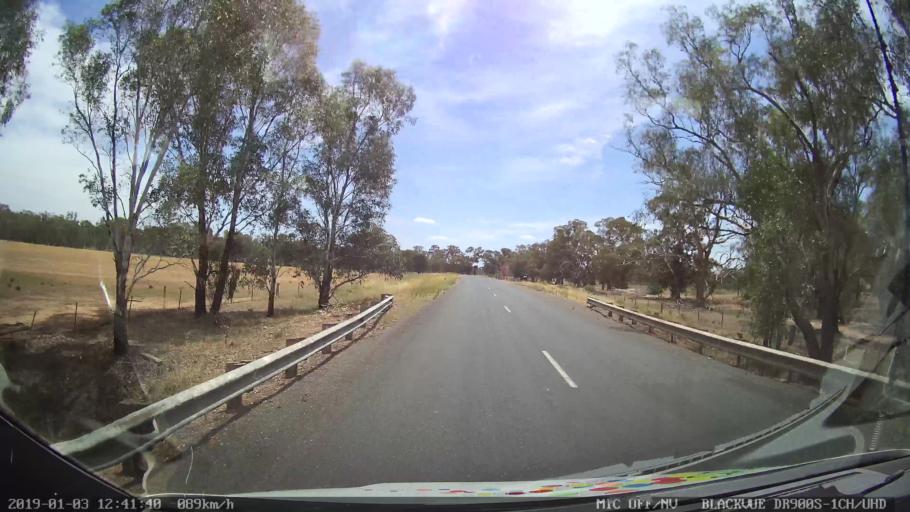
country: AU
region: New South Wales
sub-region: Weddin
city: Grenfell
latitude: -33.7967
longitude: 148.2153
